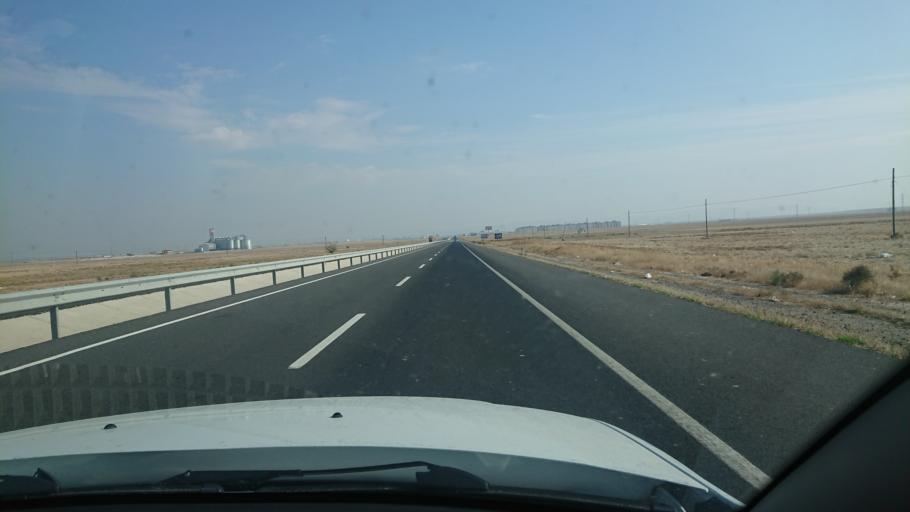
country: TR
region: Aksaray
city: Yesilova
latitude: 38.3287
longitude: 33.8987
